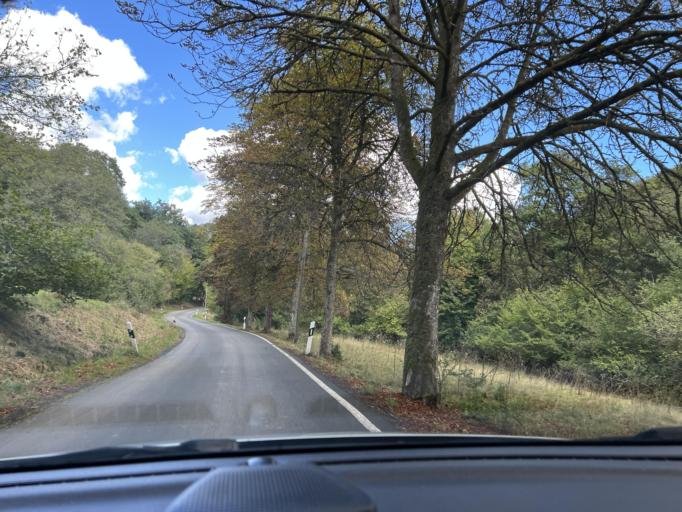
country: DE
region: North Rhine-Westphalia
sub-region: Regierungsbezirk Arnsberg
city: Bad Laasphe
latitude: 50.9571
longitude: 8.4045
